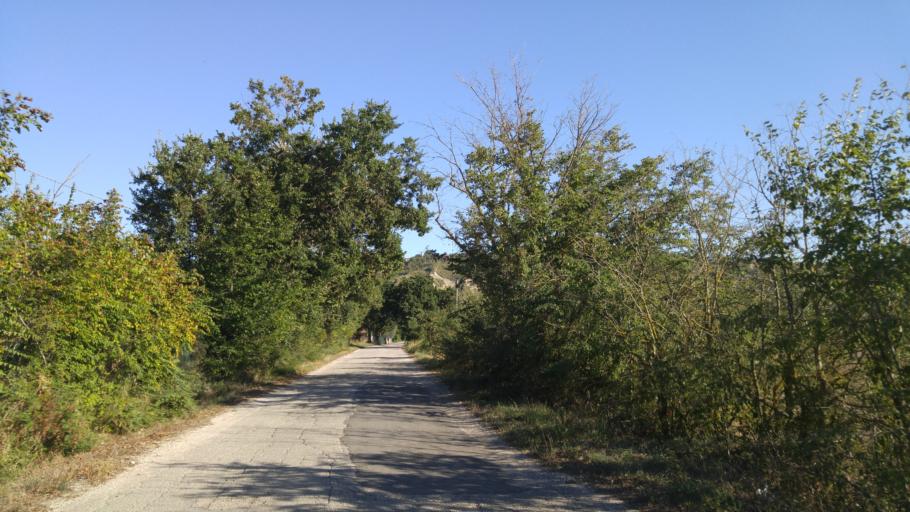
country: IT
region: The Marches
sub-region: Provincia di Pesaro e Urbino
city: Bellocchi
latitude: 43.7735
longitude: 12.9867
